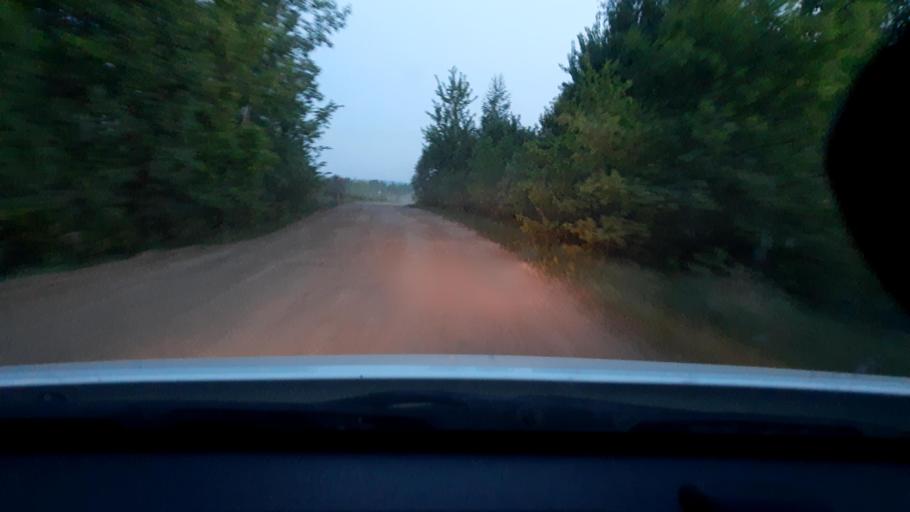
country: RU
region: Bashkortostan
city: Avdon
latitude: 54.5242
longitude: 55.8268
